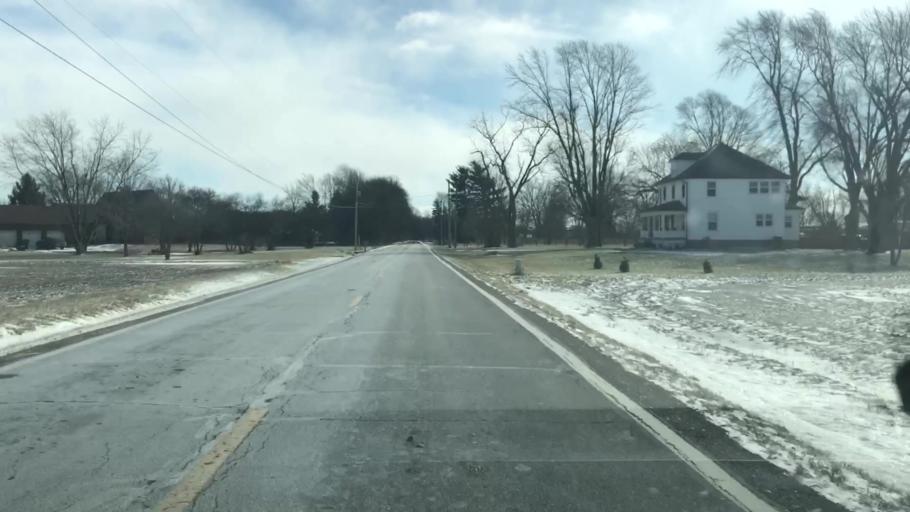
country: US
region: Ohio
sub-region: Franklin County
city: Hilliard
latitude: 40.0234
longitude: -83.2223
